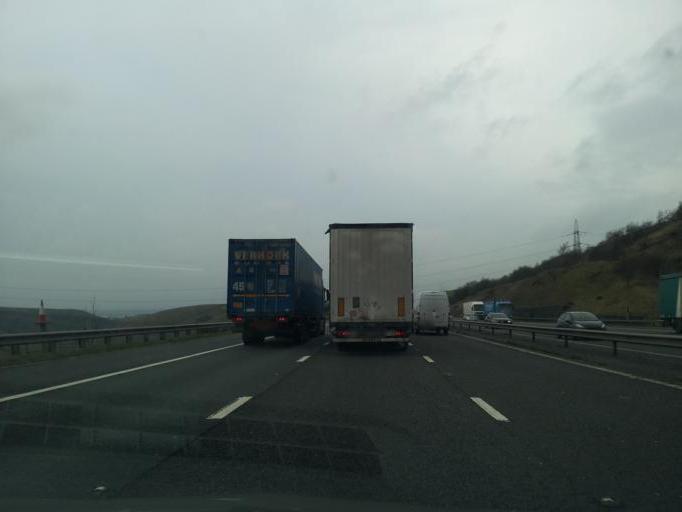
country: GB
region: England
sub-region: Borough of Rochdale
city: Littleborough
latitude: 53.6244
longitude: -2.0636
